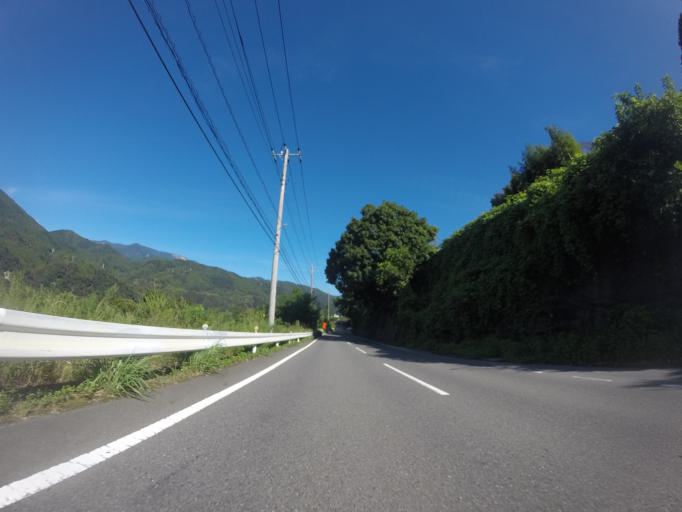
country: JP
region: Shizuoka
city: Fujinomiya
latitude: 35.3188
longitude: 138.4532
